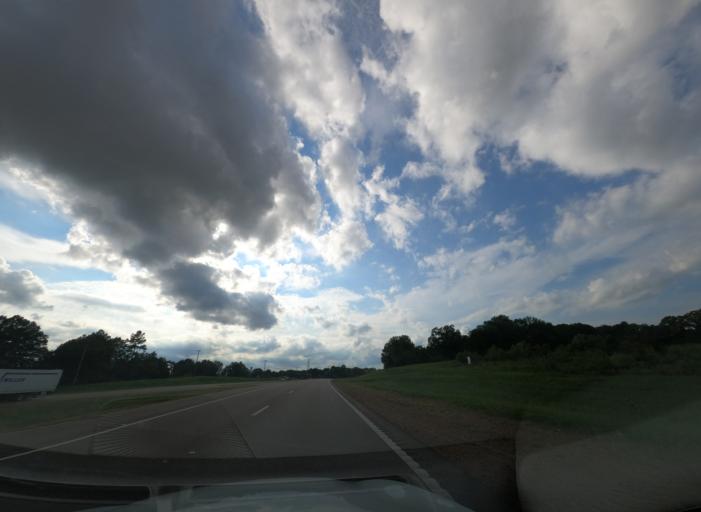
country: US
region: Tennessee
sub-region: Fayette County
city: Piperton
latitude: 34.9888
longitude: -89.6078
